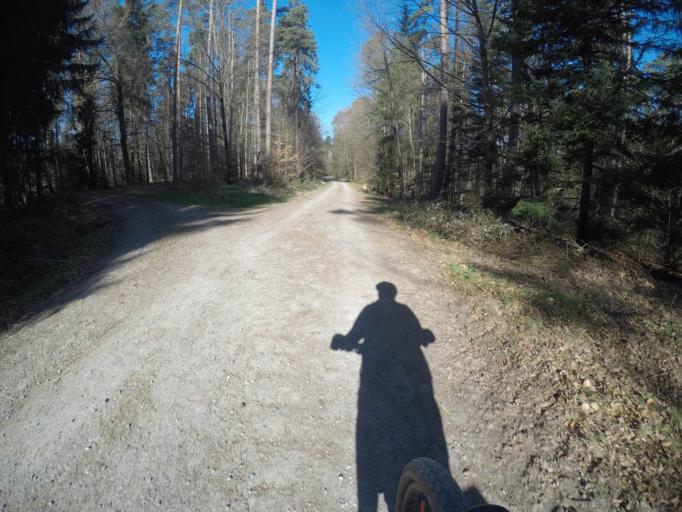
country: DE
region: Baden-Wuerttemberg
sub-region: Tuebingen Region
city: Dettenhausen
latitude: 48.6046
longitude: 9.1214
